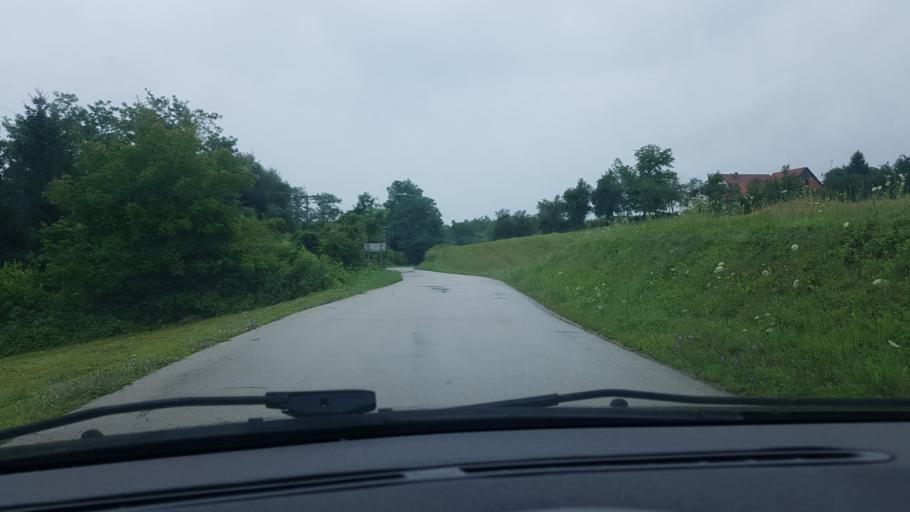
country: HR
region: Licko-Senjska
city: Jezerce
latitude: 44.9936
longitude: 15.6544
